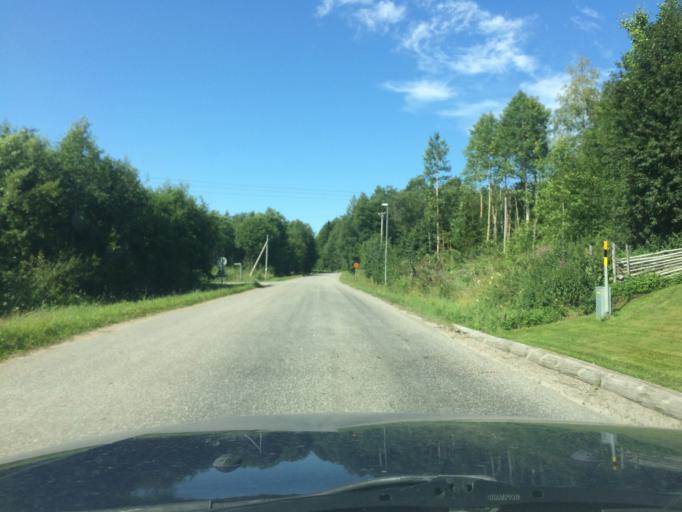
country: SE
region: Norrbotten
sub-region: Pitea Kommun
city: Norrfjarden
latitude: 65.3686
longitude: 21.4053
